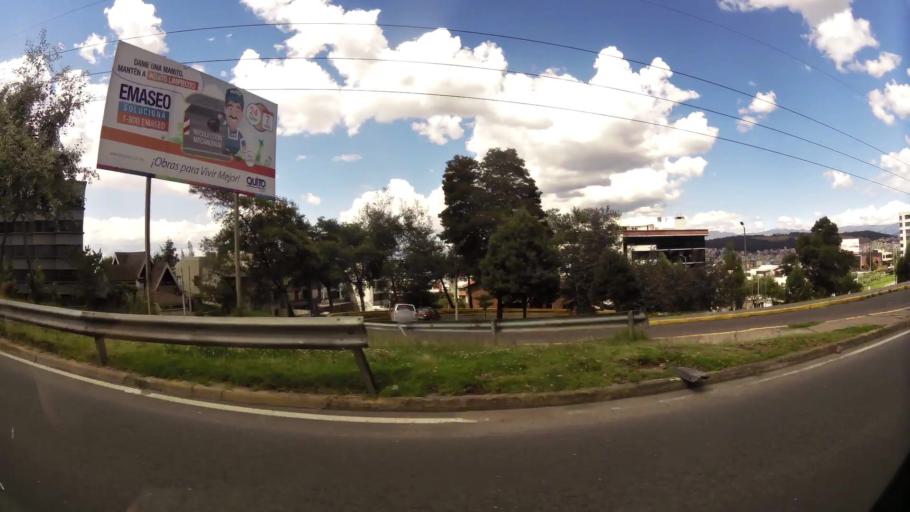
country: EC
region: Pichincha
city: Quito
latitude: -0.1606
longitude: -78.4958
